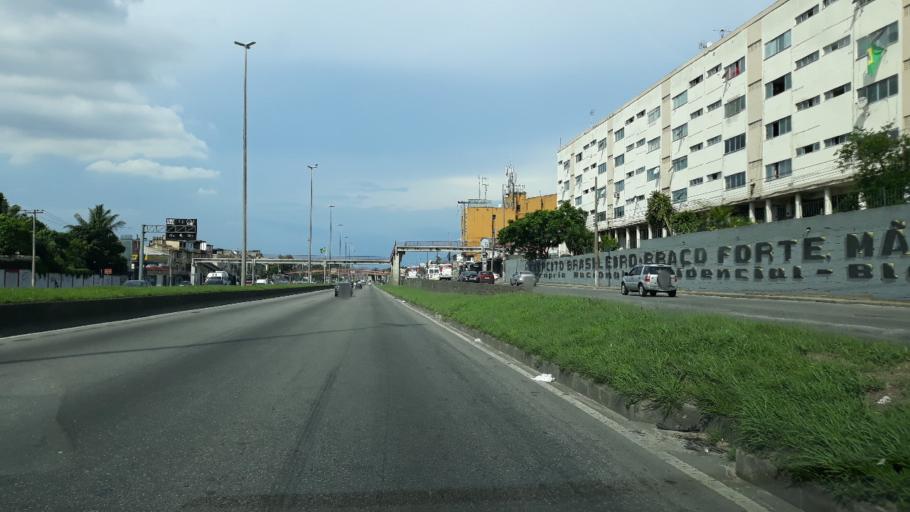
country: BR
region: Rio de Janeiro
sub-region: Sao Joao De Meriti
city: Sao Joao de Meriti
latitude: -22.8474
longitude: -43.3809
